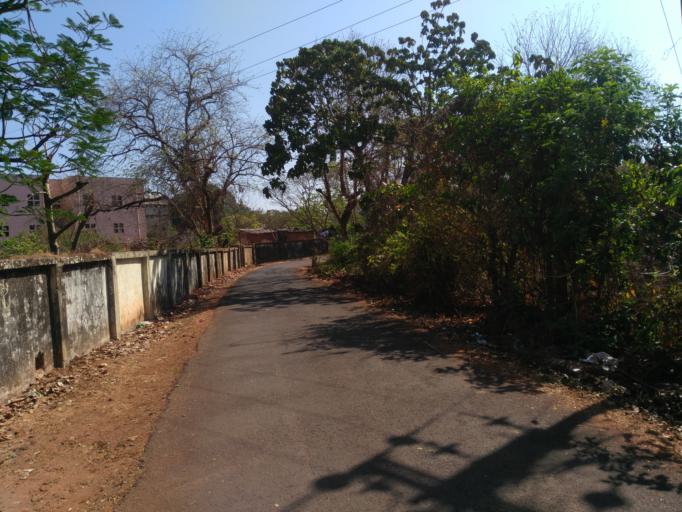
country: IN
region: Maharashtra
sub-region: Ratnagiri
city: Ratnagiri
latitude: 16.9822
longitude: 73.3124
